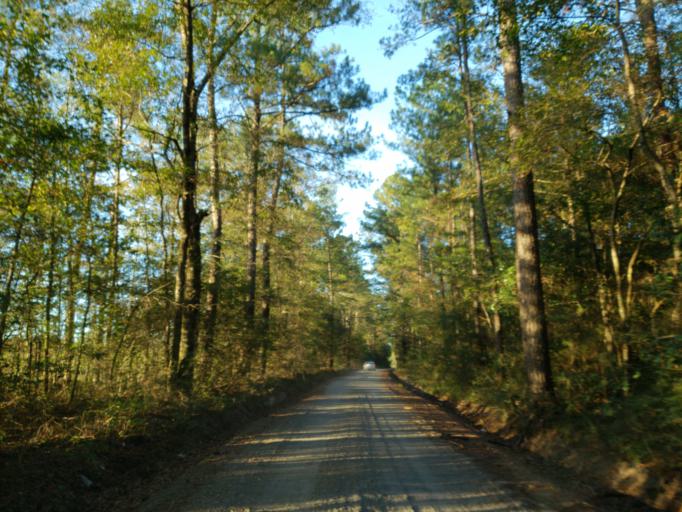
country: US
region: Mississippi
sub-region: Wayne County
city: Belmont
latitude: 31.4300
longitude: -88.5262
